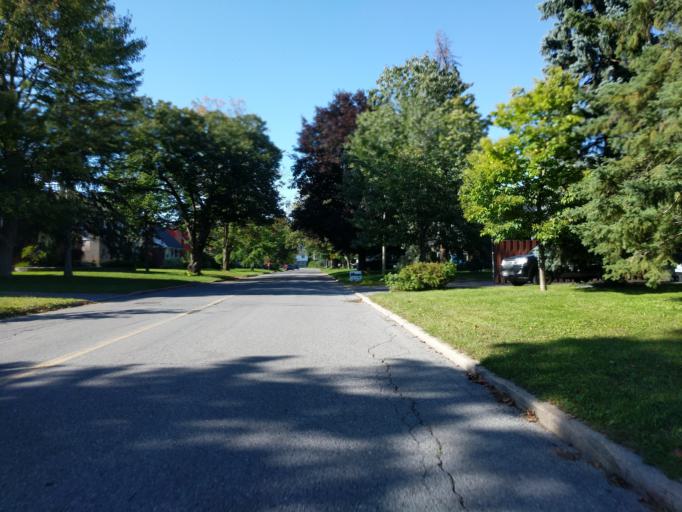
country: CA
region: Ontario
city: Bells Corners
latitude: 45.3587
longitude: -75.7655
